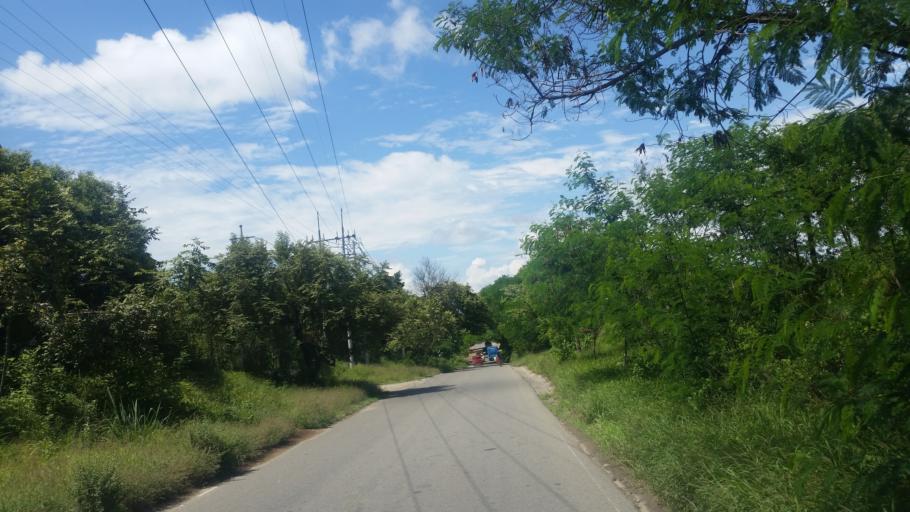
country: CO
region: Huila
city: Neiva
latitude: 2.9883
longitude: -75.2723
